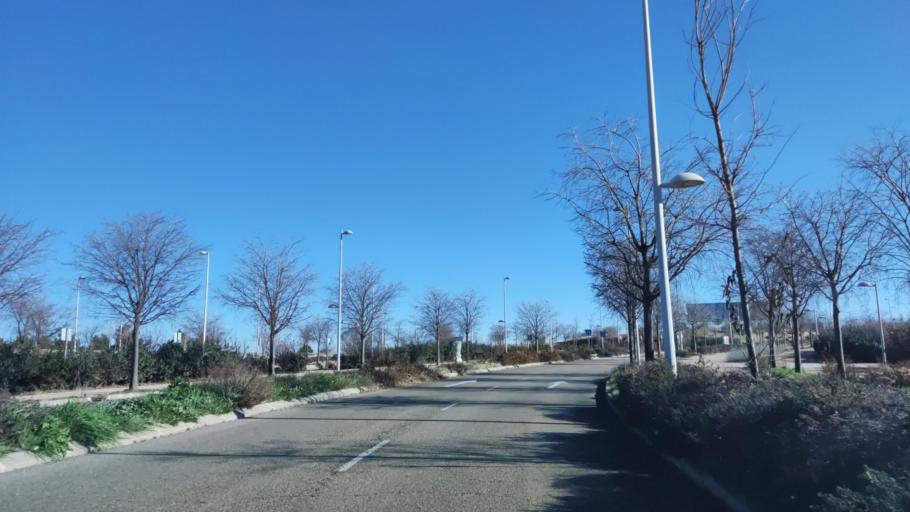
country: ES
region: Madrid
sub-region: Provincia de Madrid
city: Hortaleza
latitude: 40.4979
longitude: -3.6361
